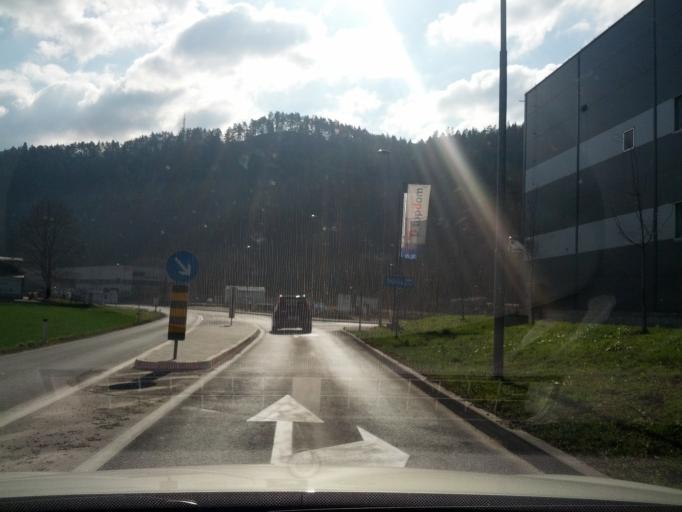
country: SI
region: Litija
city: Litija
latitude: 46.0581
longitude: 14.8166
